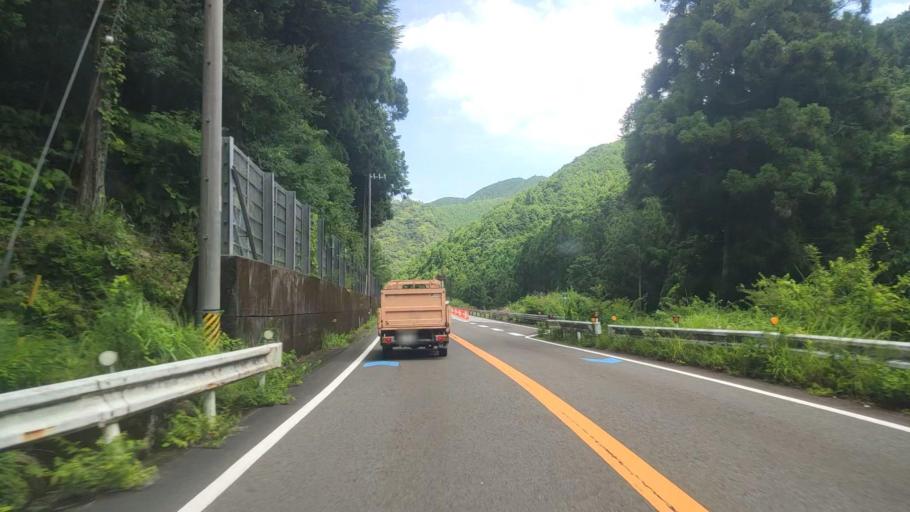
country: JP
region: Mie
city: Owase
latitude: 33.9254
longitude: 136.0925
